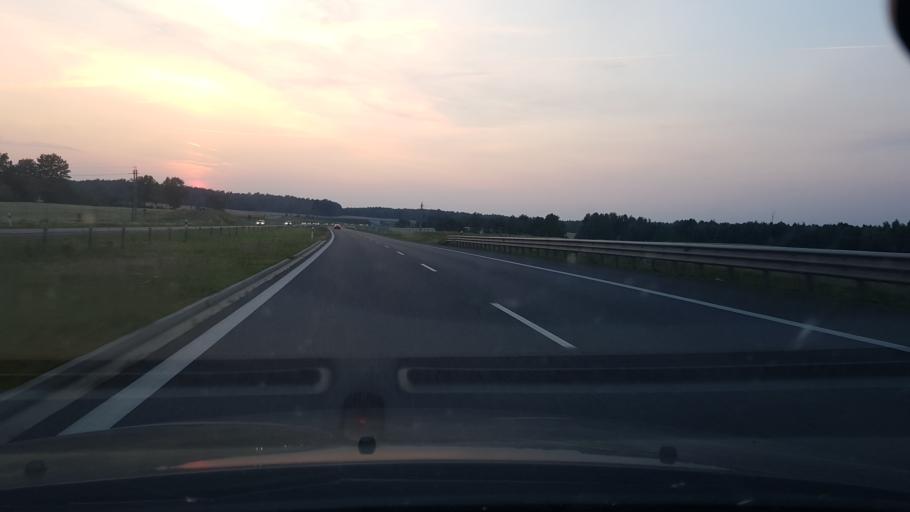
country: PL
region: Warmian-Masurian Voivodeship
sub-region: Powiat nidzicki
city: Nidzica
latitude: 53.4449
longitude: 20.3338
